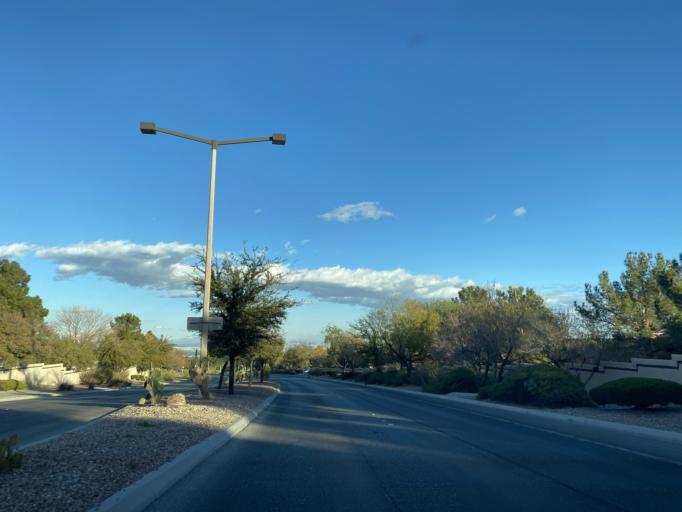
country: US
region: Nevada
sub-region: Clark County
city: Summerlin South
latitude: 36.2035
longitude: -115.3315
